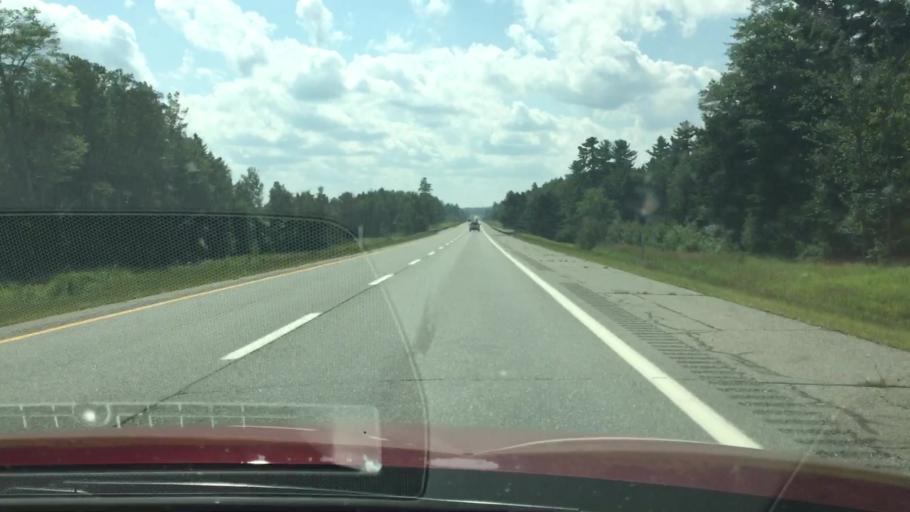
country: US
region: Maine
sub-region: Penobscot County
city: Enfield
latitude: 45.3391
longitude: -68.6258
